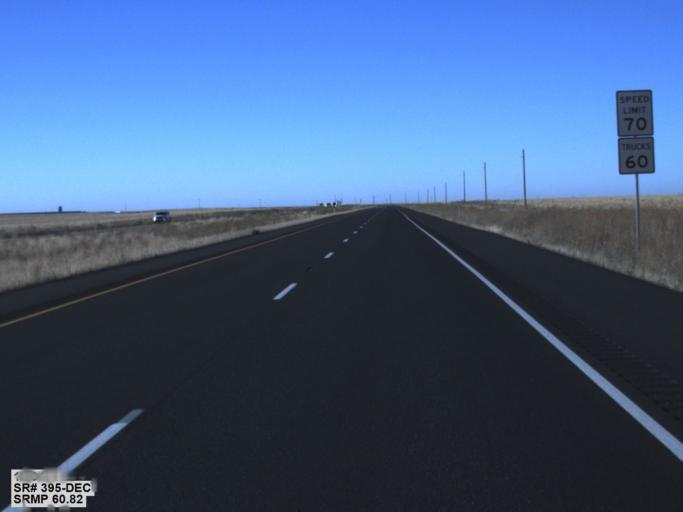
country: US
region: Washington
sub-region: Franklin County
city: Connell
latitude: 46.7308
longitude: -118.8250
